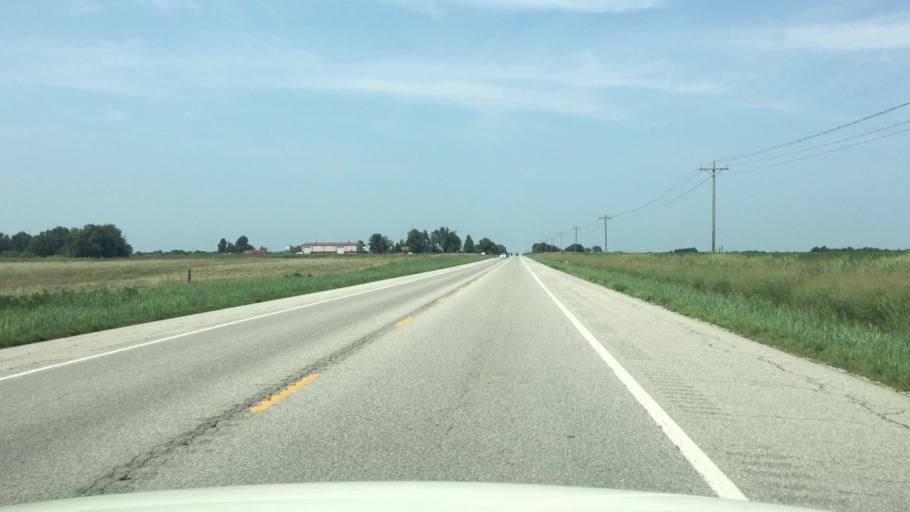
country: US
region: Kansas
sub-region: Crawford County
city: Pittsburg
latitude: 37.2671
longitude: -94.7052
